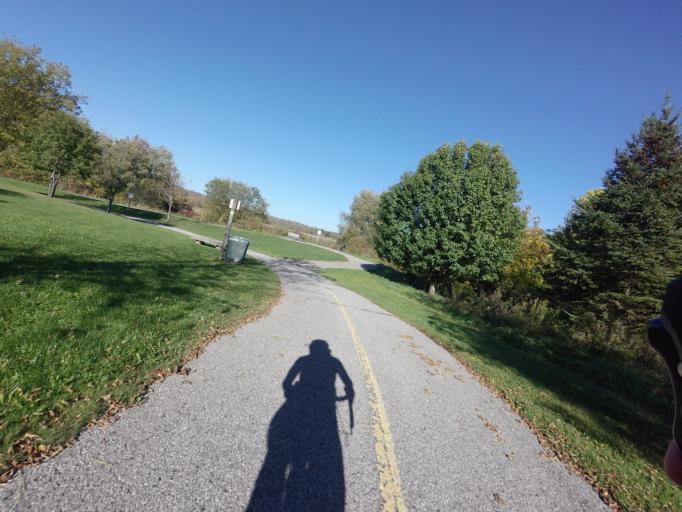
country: CA
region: Ontario
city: Oshawa
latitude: 43.8737
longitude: -78.8188
